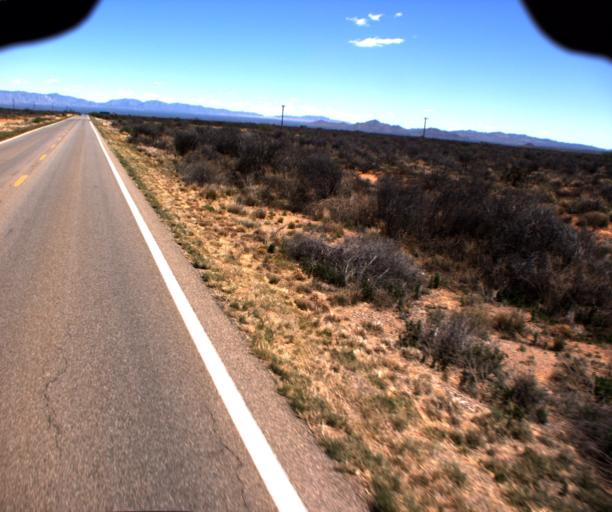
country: US
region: Arizona
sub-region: Cochise County
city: Huachuca City
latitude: 31.6998
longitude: -110.2988
